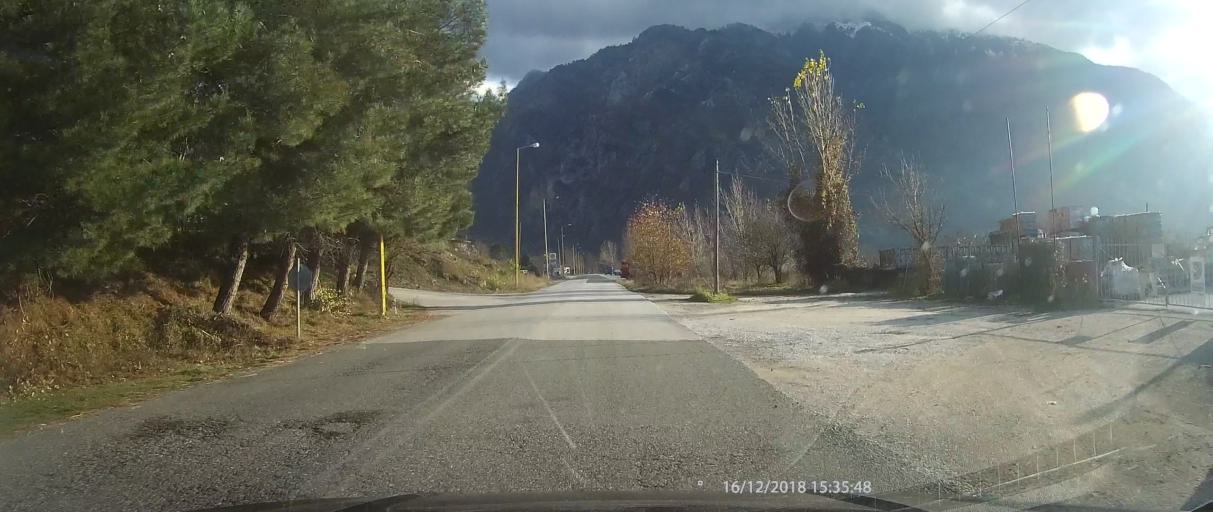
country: GR
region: Epirus
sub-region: Nomos Ioanninon
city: Konitsa
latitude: 40.0471
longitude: 20.7390
